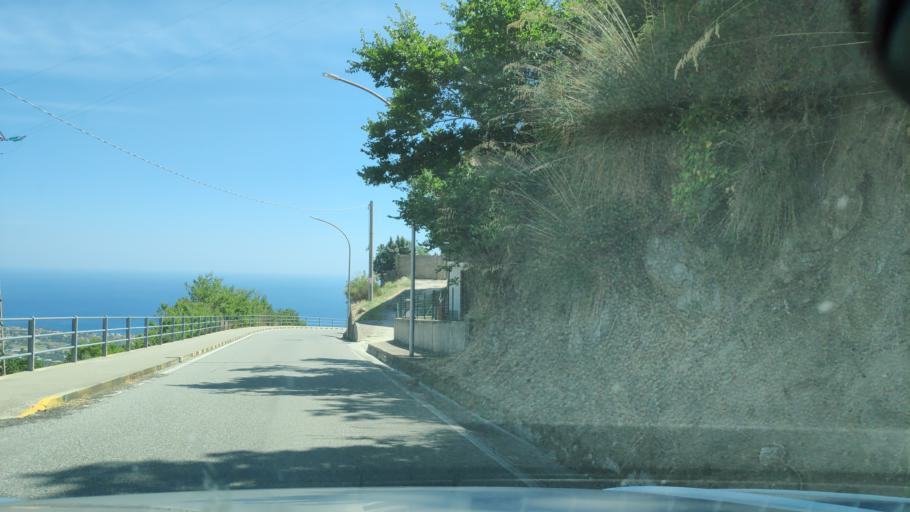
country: IT
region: Calabria
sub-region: Provincia di Catanzaro
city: Gasperina
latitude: 38.7382
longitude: 16.5111
